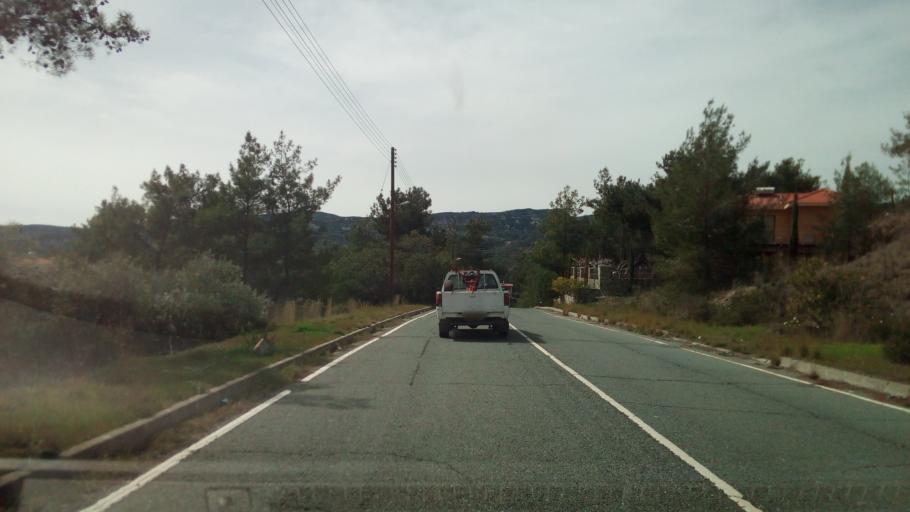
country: CY
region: Limassol
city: Pelendri
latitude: 34.8610
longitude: 32.9165
